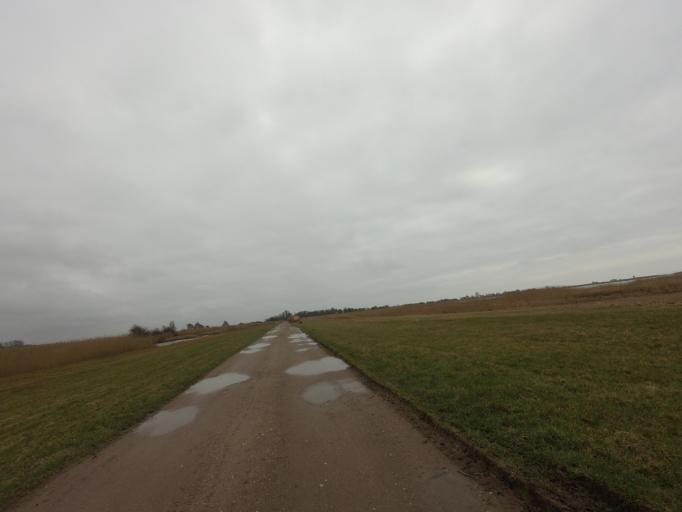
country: NL
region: Friesland
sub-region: Sudwest Fryslan
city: Makkum
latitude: 53.0451
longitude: 5.4001
